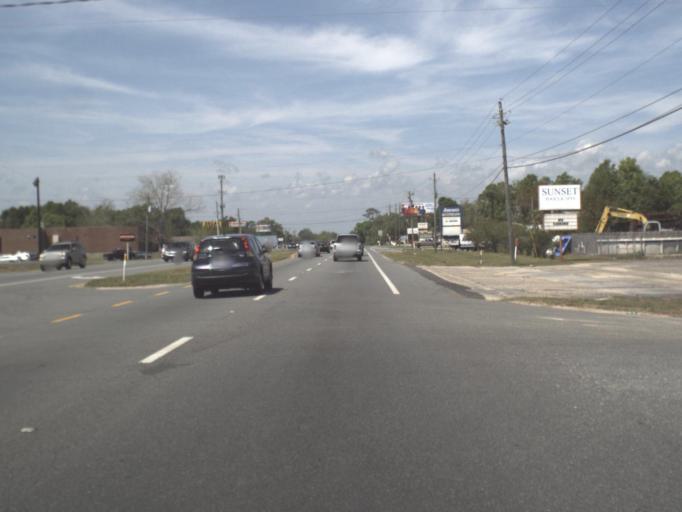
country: US
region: Florida
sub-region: Santa Rosa County
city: Pace
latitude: 30.6039
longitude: -87.1402
